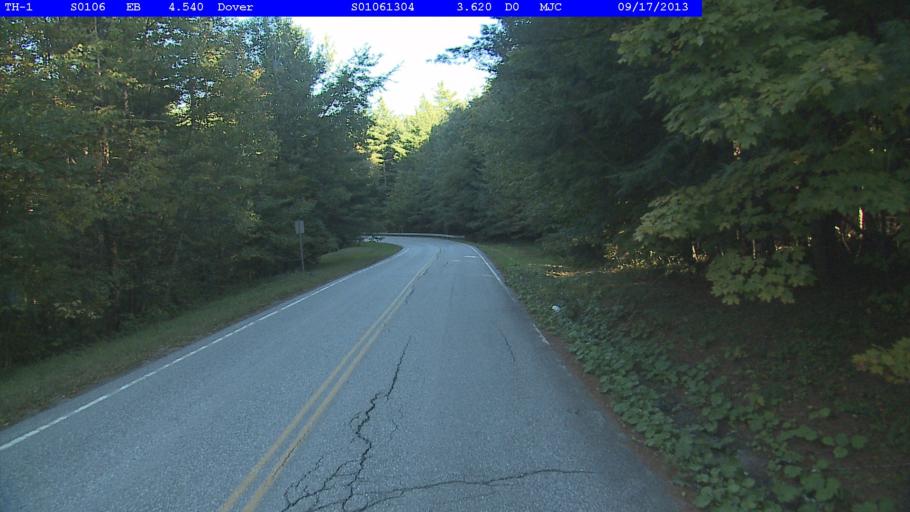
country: US
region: Vermont
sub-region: Windham County
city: Dover
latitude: 42.9449
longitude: -72.7753
